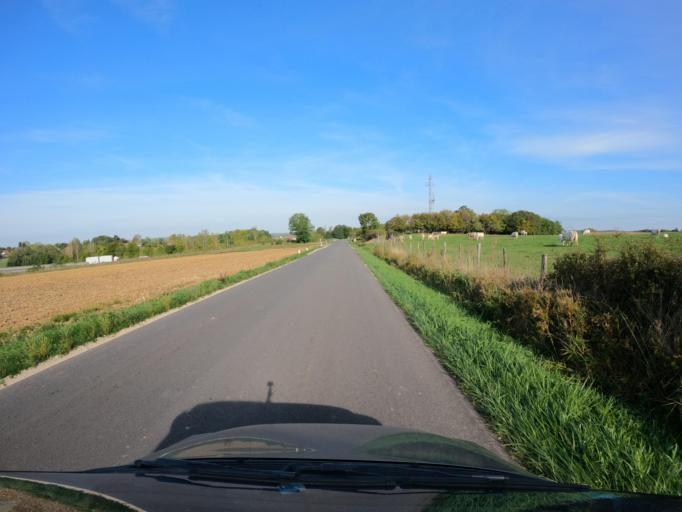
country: FR
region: Franche-Comte
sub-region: Departement du Jura
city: Montmorot
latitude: 46.7264
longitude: 5.5085
